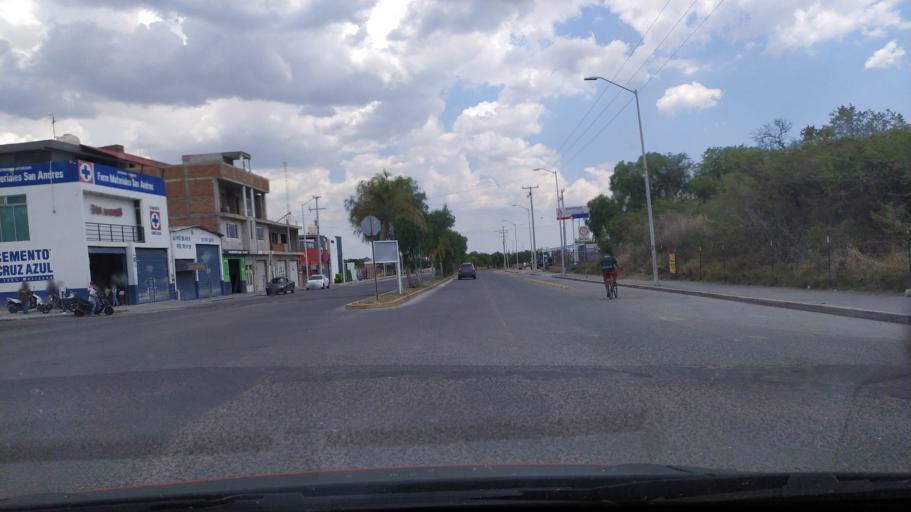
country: MX
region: Guanajuato
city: San Francisco del Rincon
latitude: 21.0443
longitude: -101.8694
